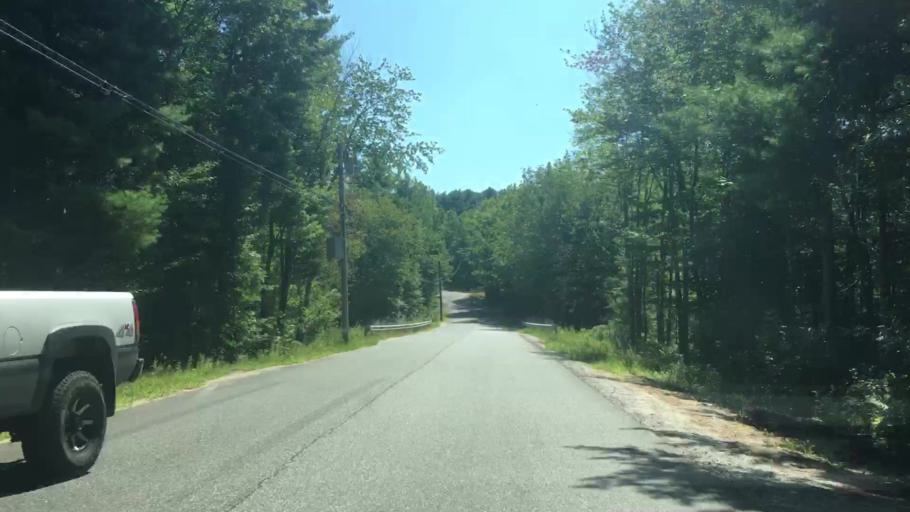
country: US
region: Maine
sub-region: Androscoggin County
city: Sabattus
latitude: 44.1208
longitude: -70.0329
